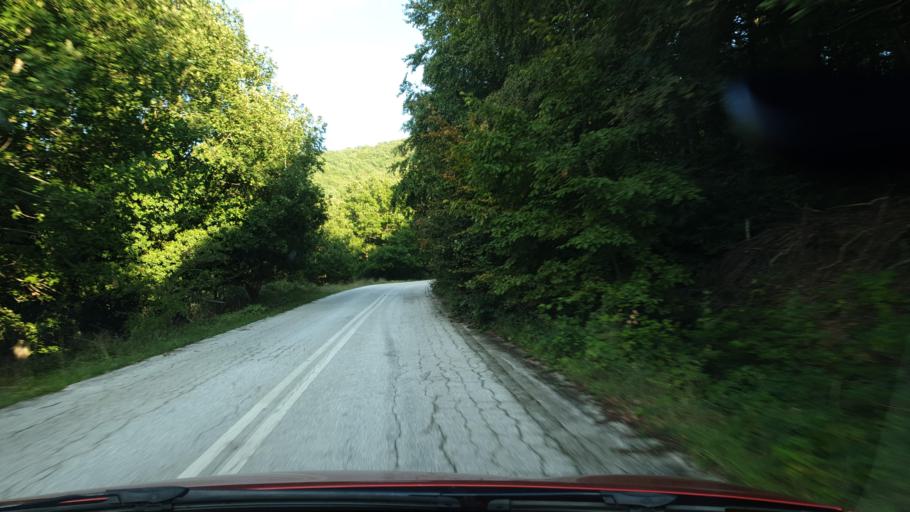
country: GR
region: Central Macedonia
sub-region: Nomos Chalkidikis
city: Galatista
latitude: 40.5072
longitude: 23.2461
